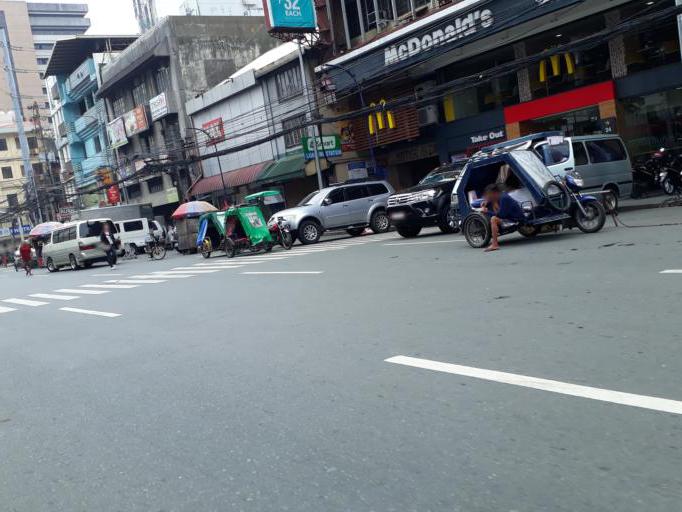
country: PH
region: Metro Manila
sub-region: City of Manila
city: Manila
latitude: 14.6006
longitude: 120.9736
